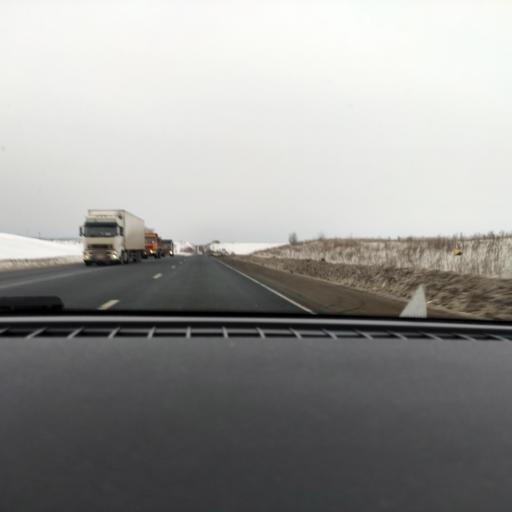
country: RU
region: Samara
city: Novosemeykino
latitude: 53.4027
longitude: 50.3935
